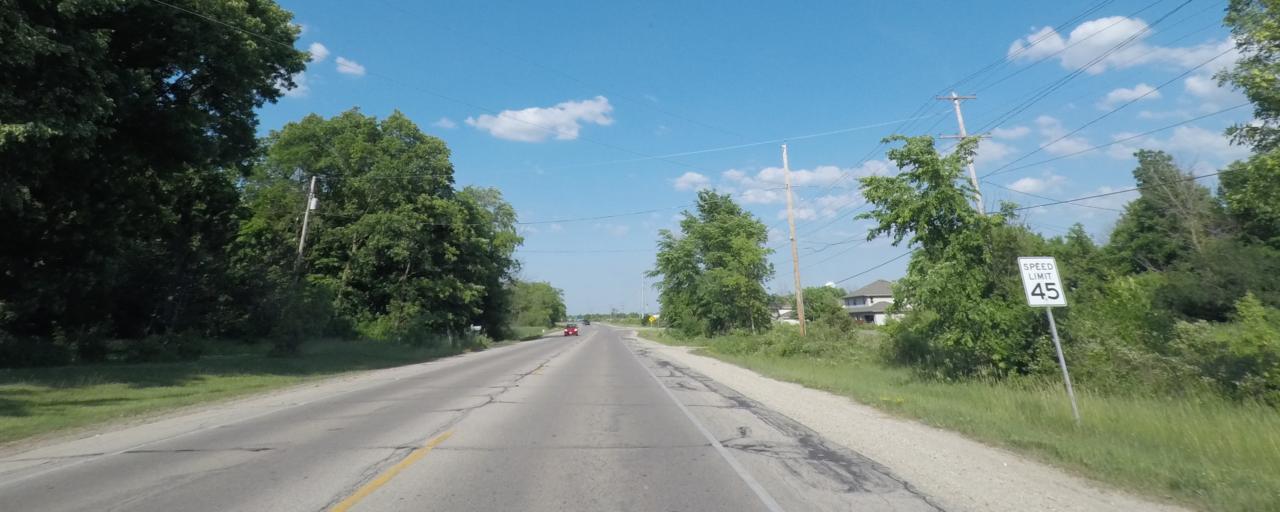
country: US
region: Wisconsin
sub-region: Waukesha County
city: Muskego
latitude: 42.8944
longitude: -88.1621
